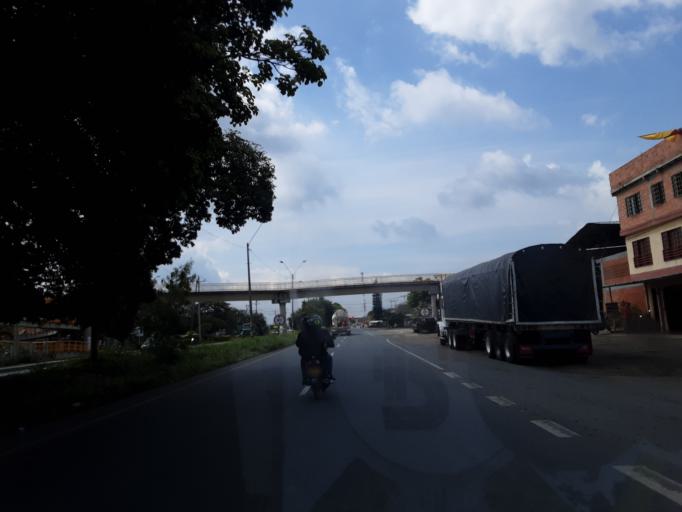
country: CO
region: Valle del Cauca
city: El Cerrito
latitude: 3.6948
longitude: -76.3151
